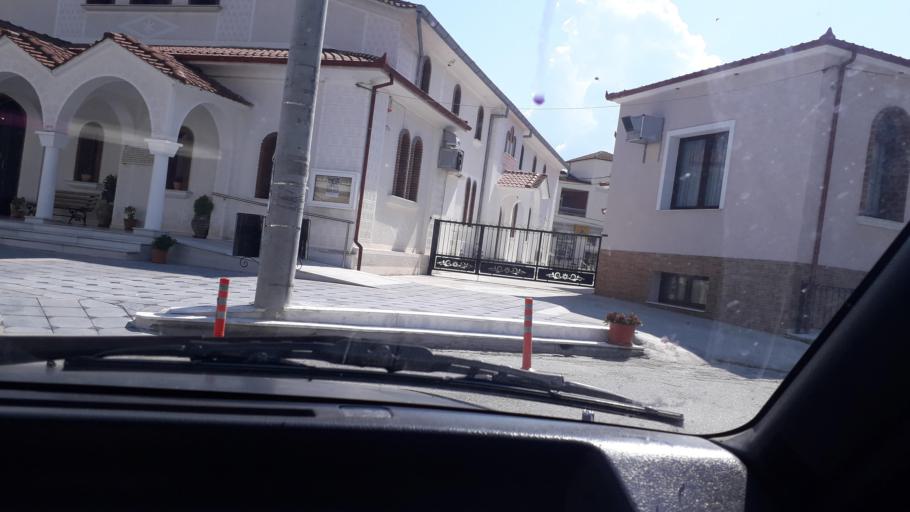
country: GR
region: Central Macedonia
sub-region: Nomos Pellis
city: Aridaia
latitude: 40.9744
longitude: 22.0608
